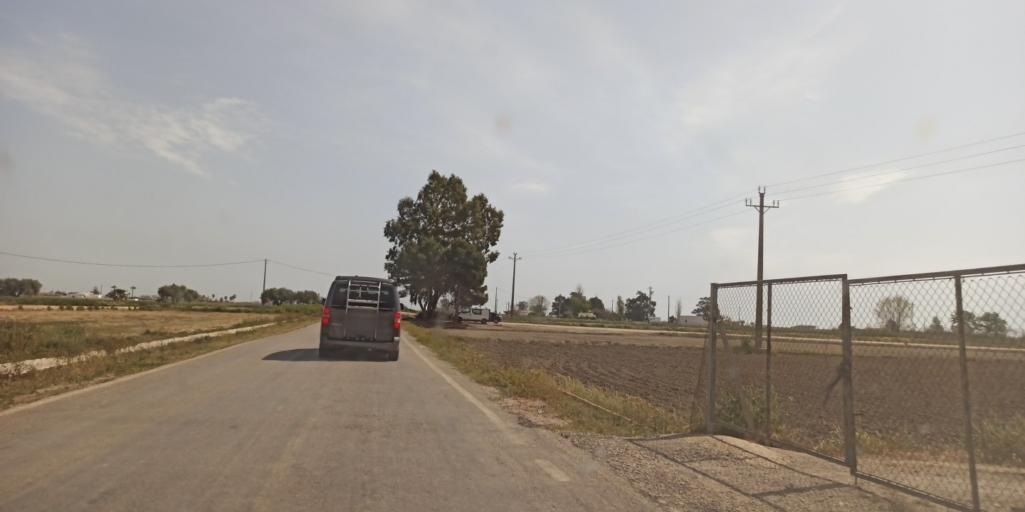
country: ES
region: Catalonia
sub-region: Provincia de Tarragona
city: Deltebre
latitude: 40.6469
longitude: 0.7059
